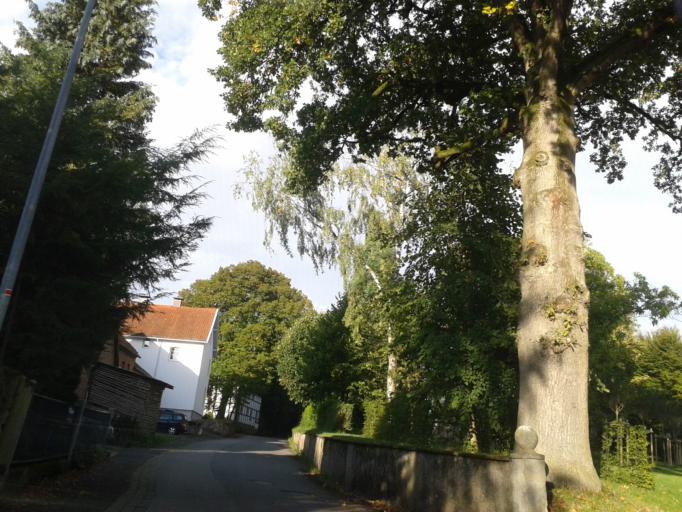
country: DE
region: North Rhine-Westphalia
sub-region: Regierungsbezirk Detmold
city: Barntrup
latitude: 51.9956
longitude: 9.0549
